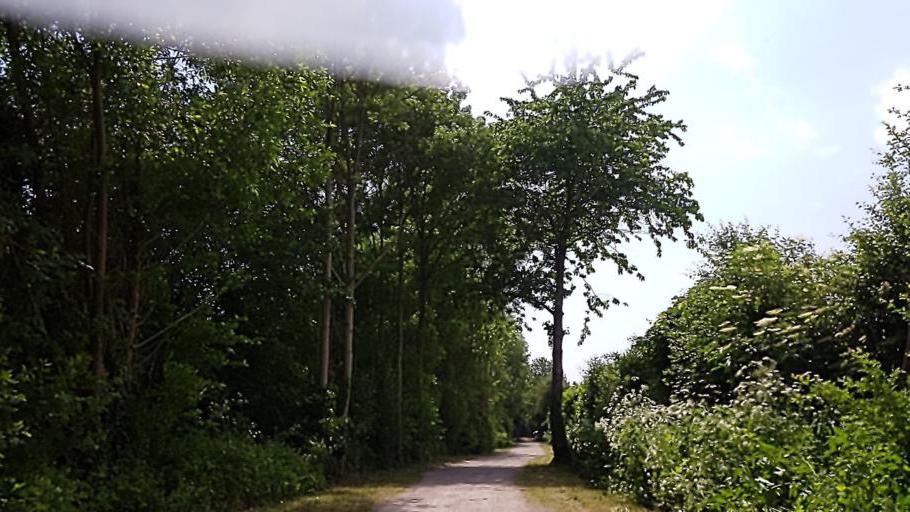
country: FR
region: Nord-Pas-de-Calais
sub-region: Departement du Nord
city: Vieux-Conde
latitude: 50.4756
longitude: 3.5716
